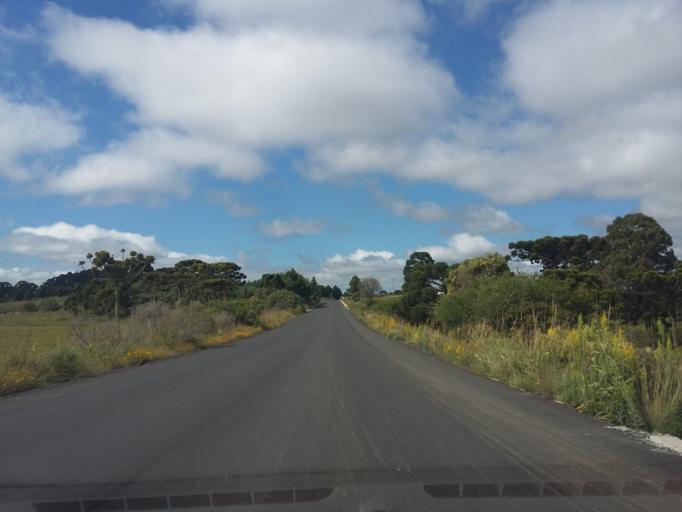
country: BR
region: Santa Catarina
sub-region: Sao Joaquim
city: Sao Joaquim
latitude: -28.0368
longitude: -50.0745
